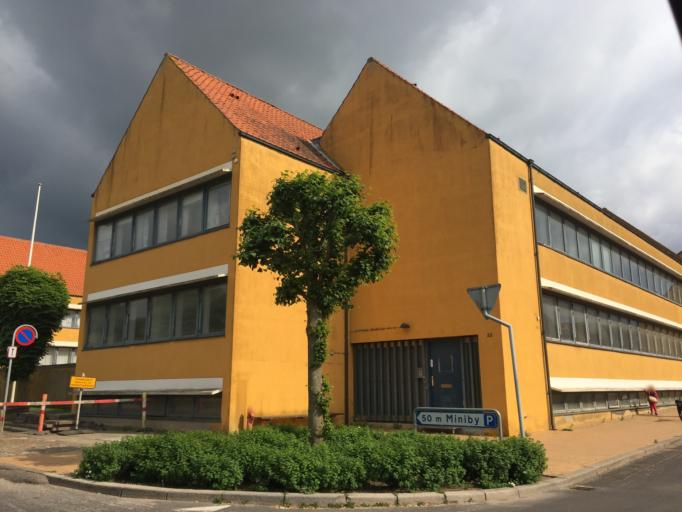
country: DK
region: South Denmark
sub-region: Assens Kommune
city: Assens
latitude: 55.2719
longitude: 9.8926
